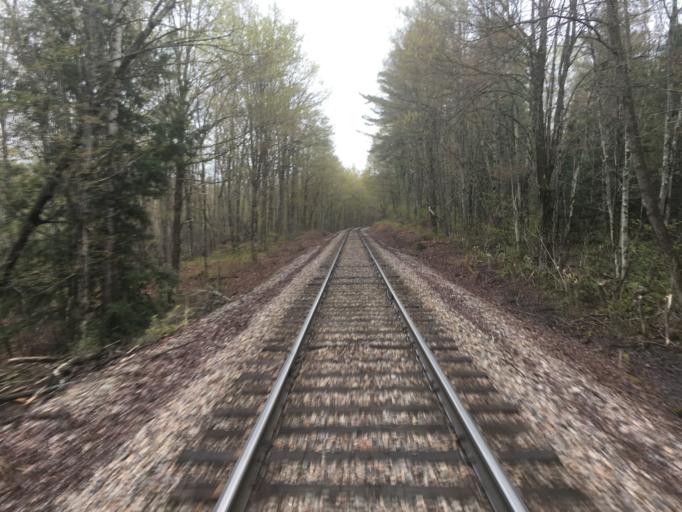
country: US
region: Vermont
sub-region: Rutland County
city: Rutland
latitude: 43.4604
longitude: -72.8764
